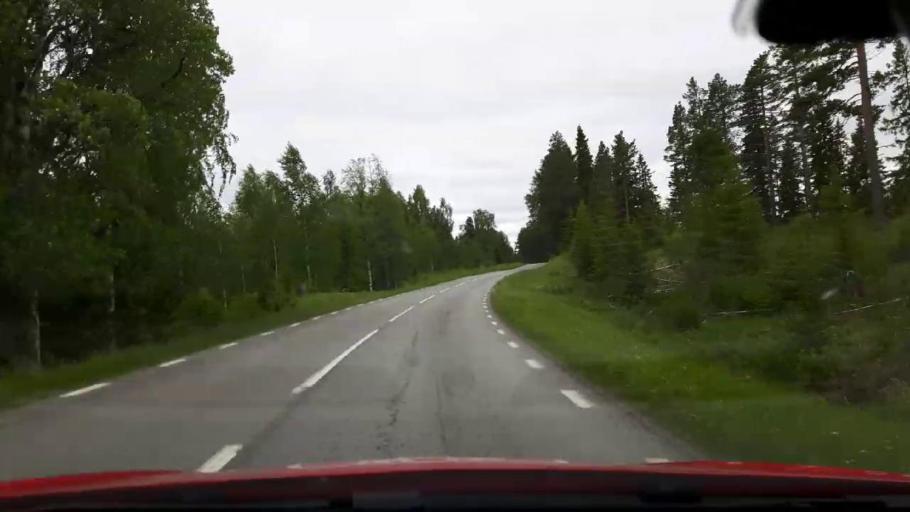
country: SE
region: Jaemtland
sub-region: Stroemsunds Kommun
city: Stroemsund
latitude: 63.4959
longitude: 15.4584
